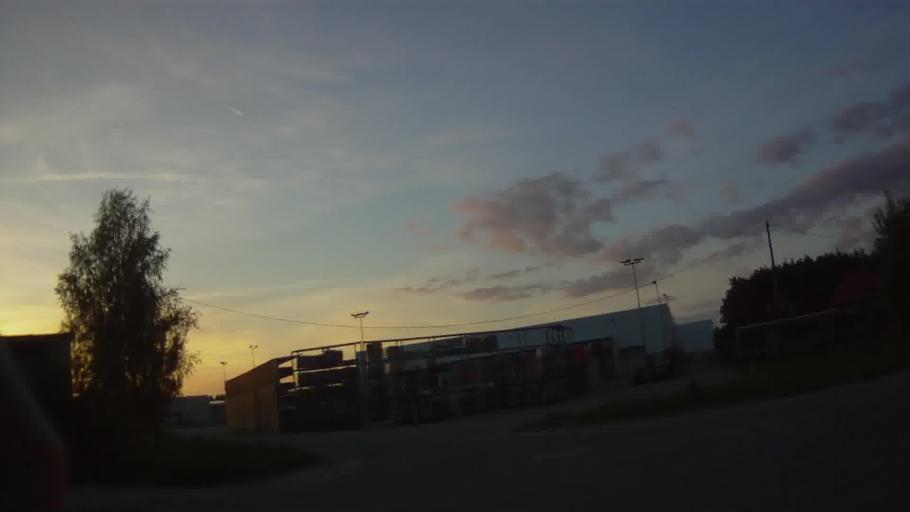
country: LV
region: Riga
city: Bergi
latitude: 57.0000
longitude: 24.2881
